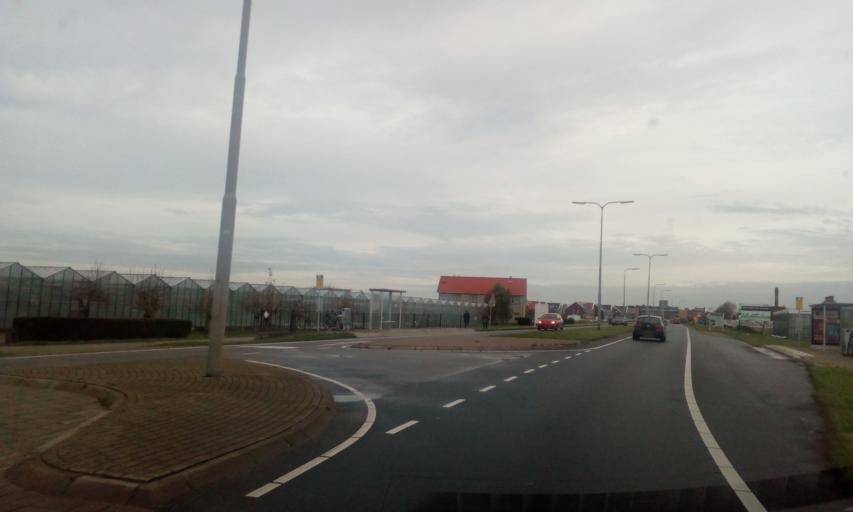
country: NL
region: South Holland
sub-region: Gemeente Westland
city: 's-Gravenzande
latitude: 52.0180
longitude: 4.1578
